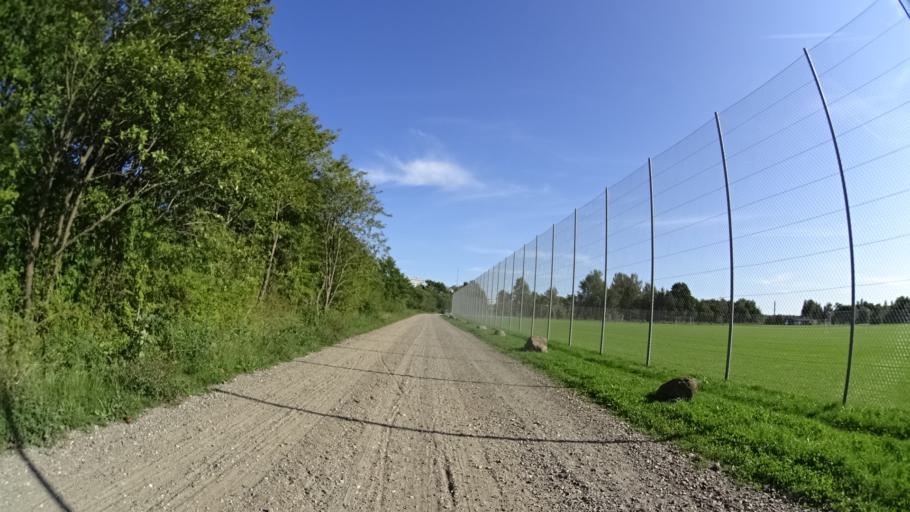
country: DK
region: Central Jutland
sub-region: Arhus Kommune
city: Arhus
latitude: 56.1473
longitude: 10.1714
